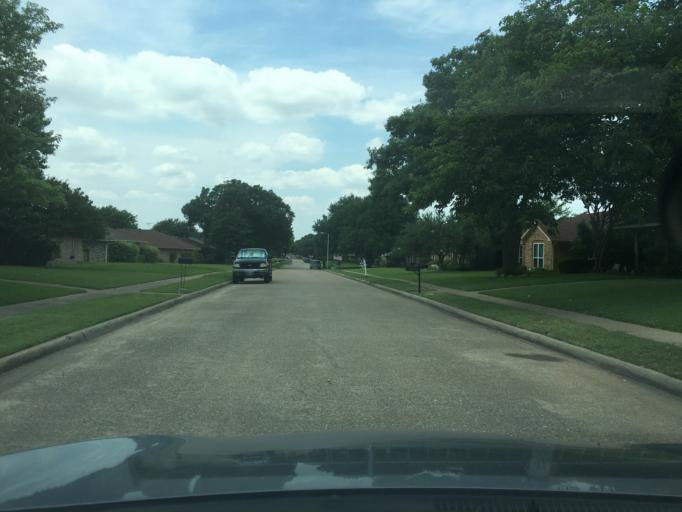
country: US
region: Texas
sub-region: Dallas County
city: Richardson
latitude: 32.9574
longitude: -96.6879
